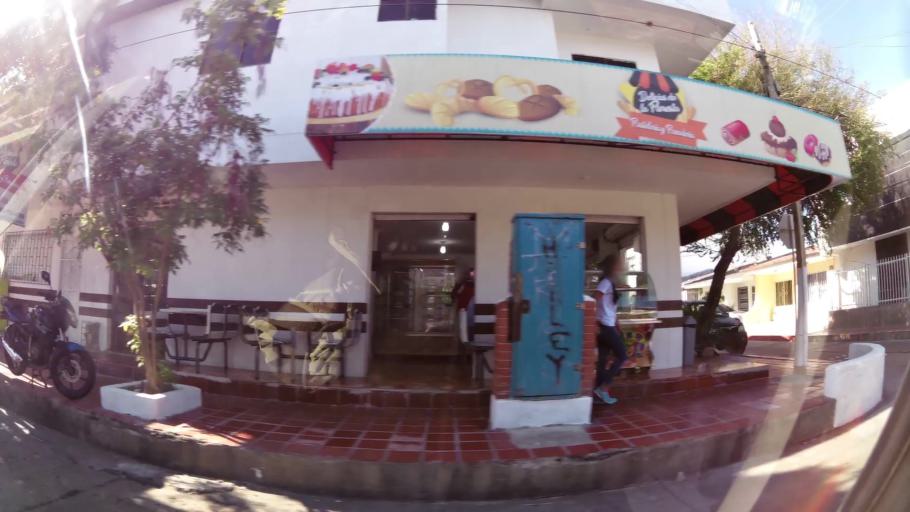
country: CO
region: Atlantico
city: Barranquilla
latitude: 11.0230
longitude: -74.8092
